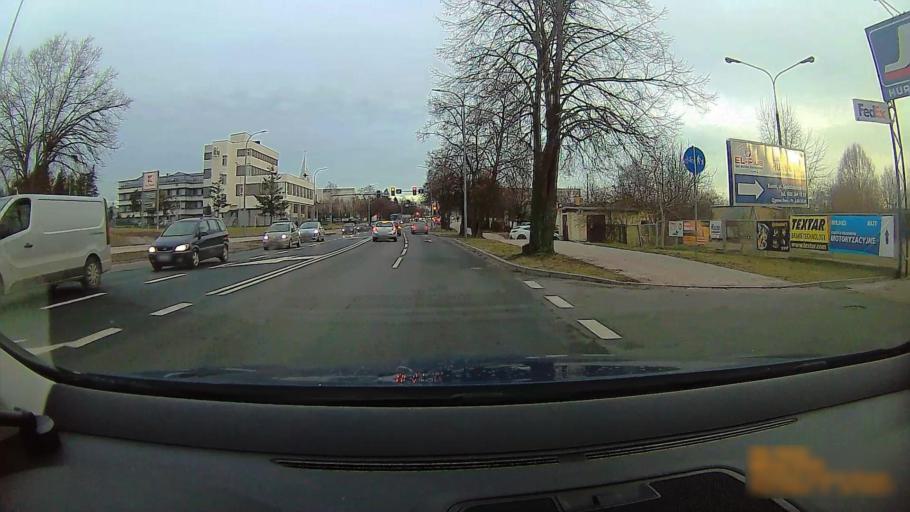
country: PL
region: Greater Poland Voivodeship
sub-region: Konin
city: Konin
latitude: 52.2305
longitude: 18.2395
